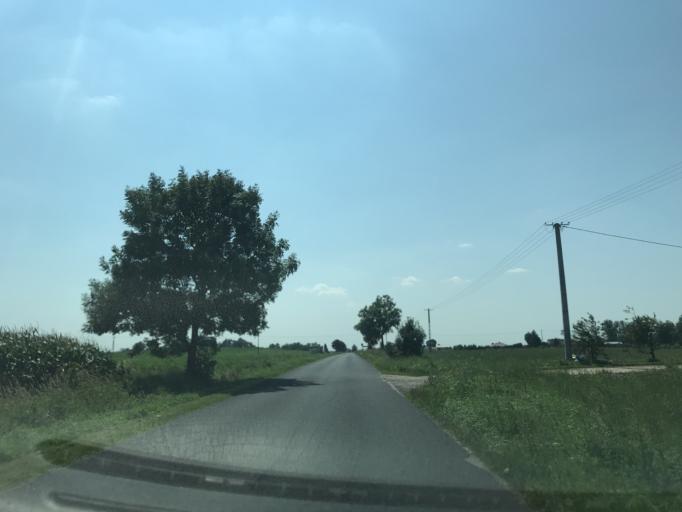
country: PL
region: Kujawsko-Pomorskie
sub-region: Powiat lipnowski
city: Kikol
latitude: 52.9278
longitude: 19.1849
